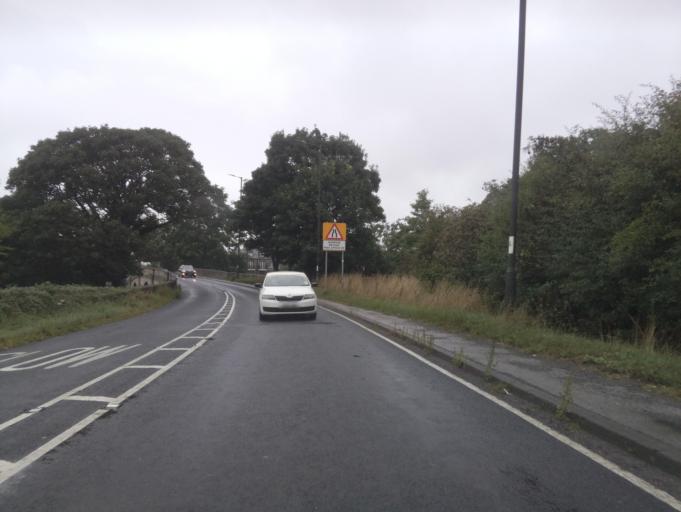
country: GB
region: England
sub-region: North Yorkshire
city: Pannal
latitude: 53.9091
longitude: -1.5259
